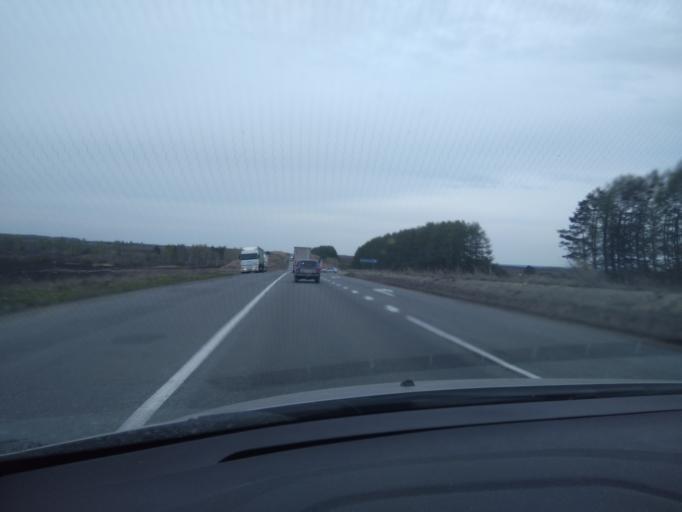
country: RU
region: Sverdlovsk
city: Kamyshlov
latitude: 56.8691
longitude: 62.9315
